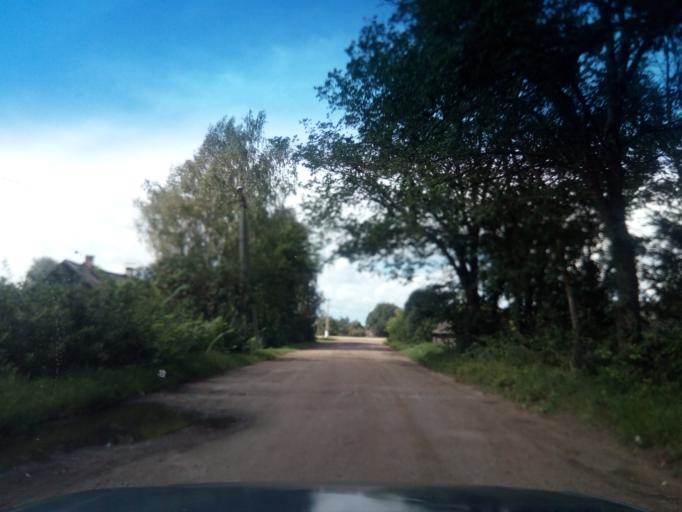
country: BY
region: Vitebsk
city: Dzisna
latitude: 55.6744
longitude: 28.3327
